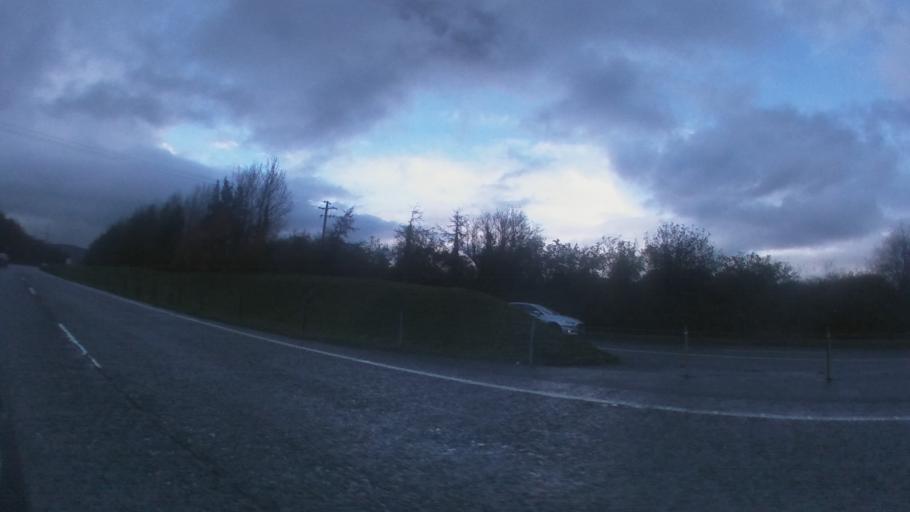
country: IE
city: Newtownmountkennedy
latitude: 53.0897
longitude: -6.1112
